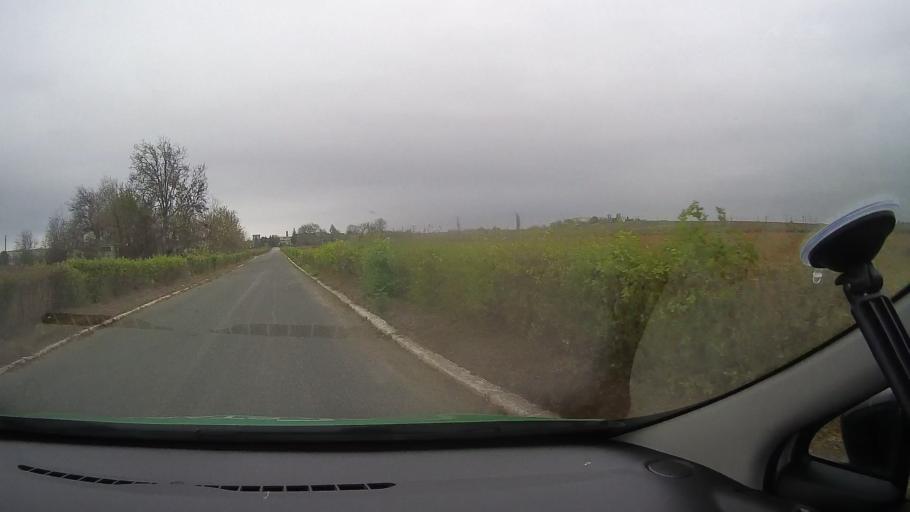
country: RO
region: Constanta
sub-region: Oras Murfatlar
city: Murfatlar
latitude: 44.1729
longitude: 28.4226
